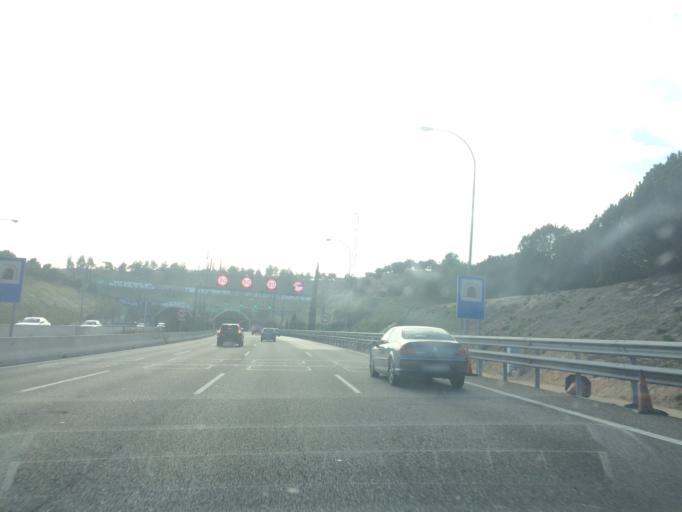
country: ES
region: Madrid
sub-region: Provincia de Madrid
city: Fuencarral-El Pardo
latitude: 40.4887
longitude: -3.7406
